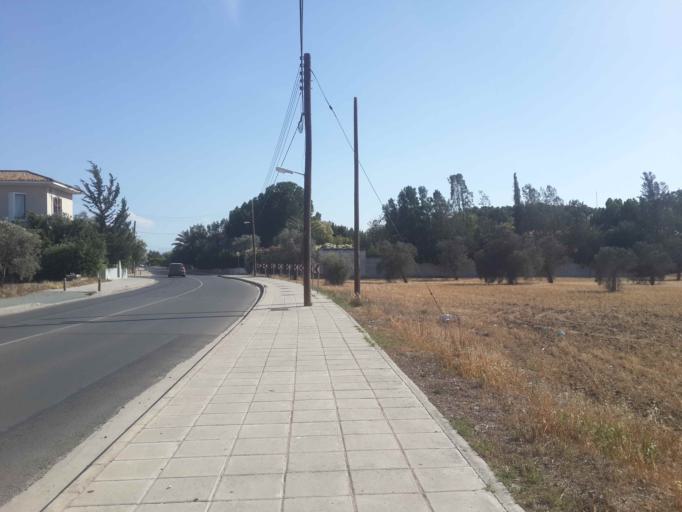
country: CY
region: Lefkosia
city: Nicosia
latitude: 35.1509
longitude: 33.3353
